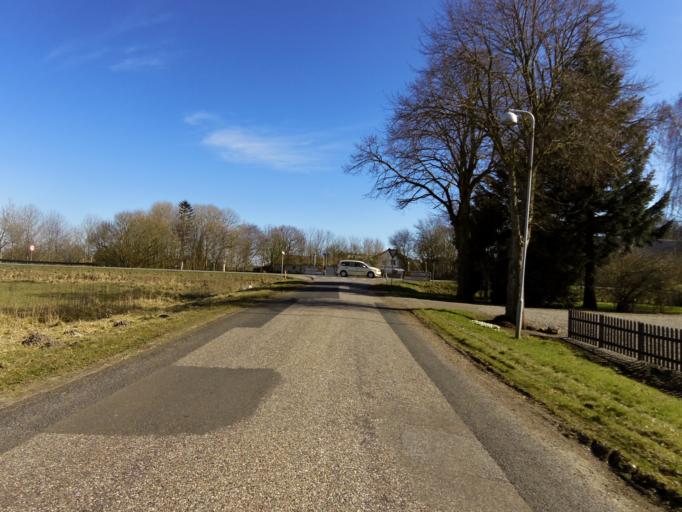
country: DK
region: South Denmark
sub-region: Tonder Kommune
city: Toftlund
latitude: 55.2347
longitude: 9.1227
